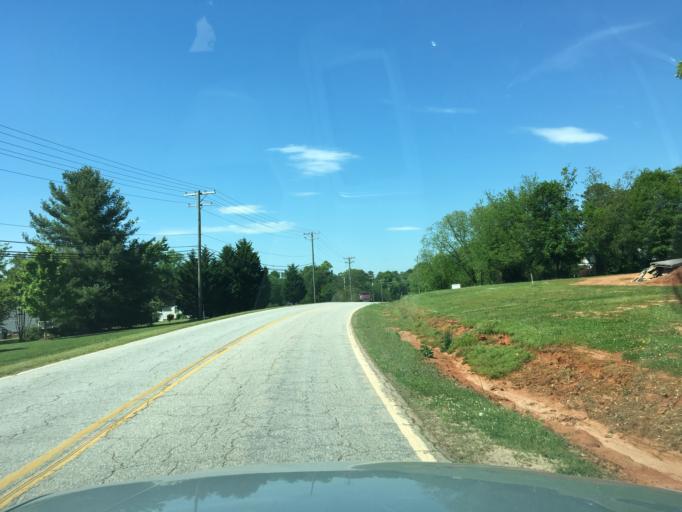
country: US
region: South Carolina
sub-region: Spartanburg County
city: Fairforest
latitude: 34.9710
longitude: -82.0335
